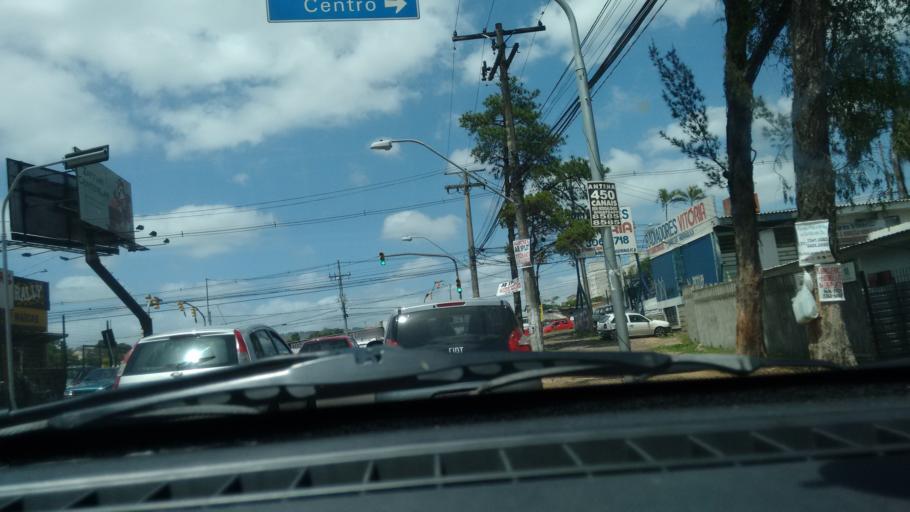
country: BR
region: Rio Grande do Sul
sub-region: Cachoeirinha
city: Cachoeirinha
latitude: -30.0110
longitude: -51.1285
